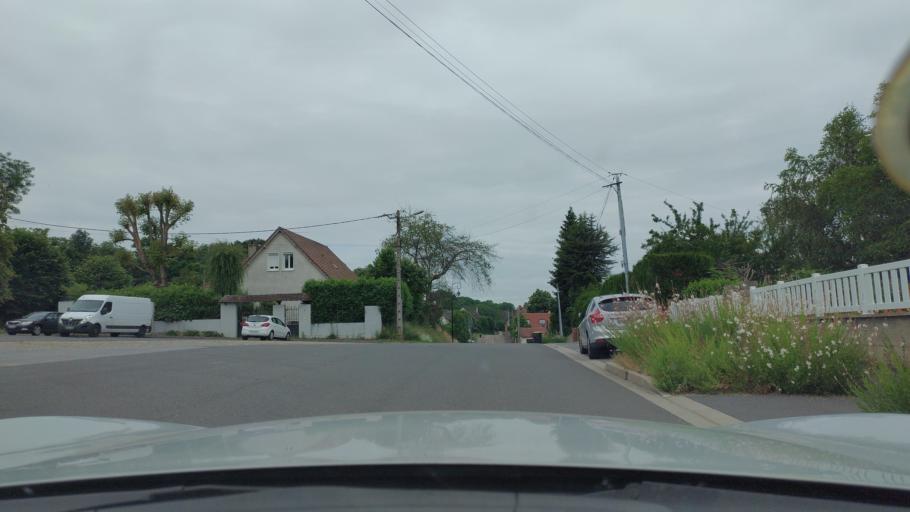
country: FR
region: Picardie
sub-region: Departement de l'Oise
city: Betz
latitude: 49.1533
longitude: 2.9553
